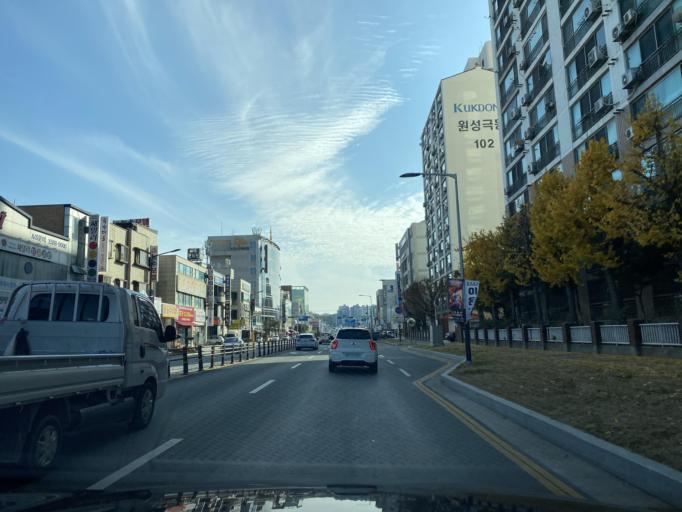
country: KR
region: Chungcheongnam-do
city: Cheonan
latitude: 36.8024
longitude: 127.1589
